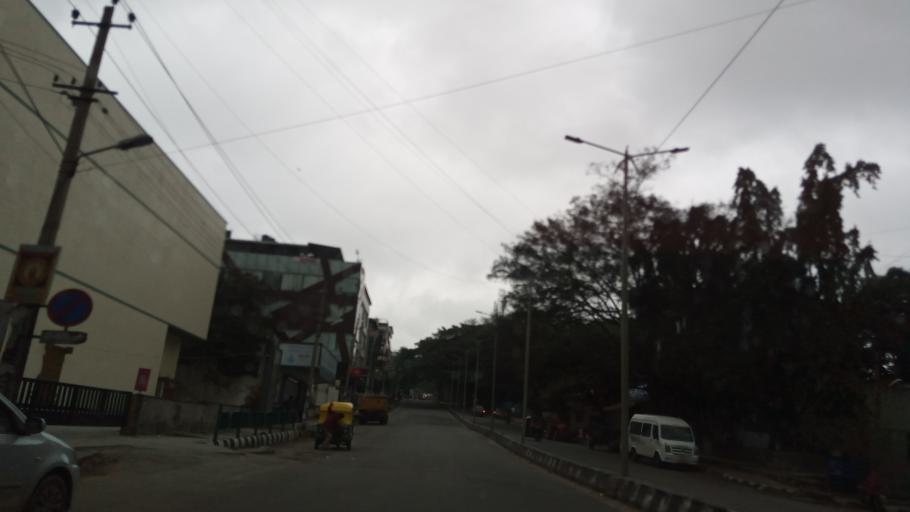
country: IN
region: Karnataka
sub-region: Bangalore Urban
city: Bangalore
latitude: 12.9225
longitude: 77.5603
